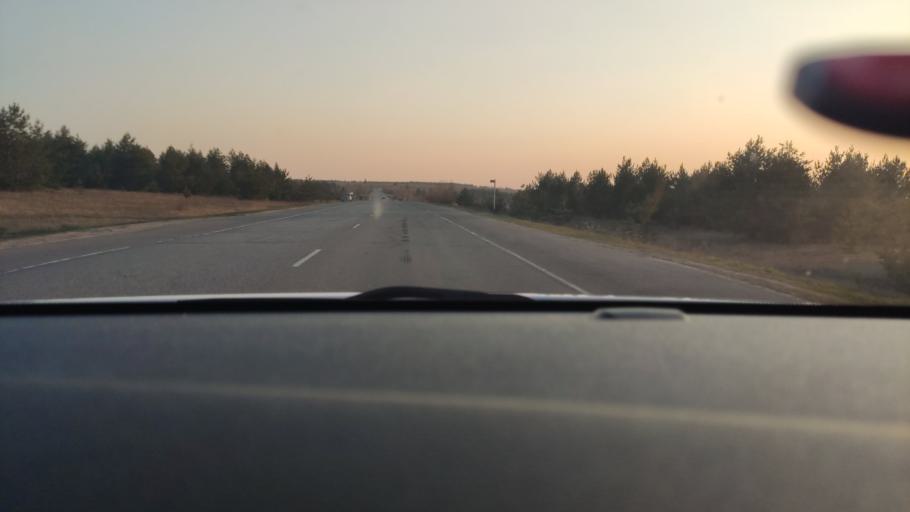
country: RU
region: Voronezj
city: Kolodeznyy
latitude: 51.3829
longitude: 39.2197
